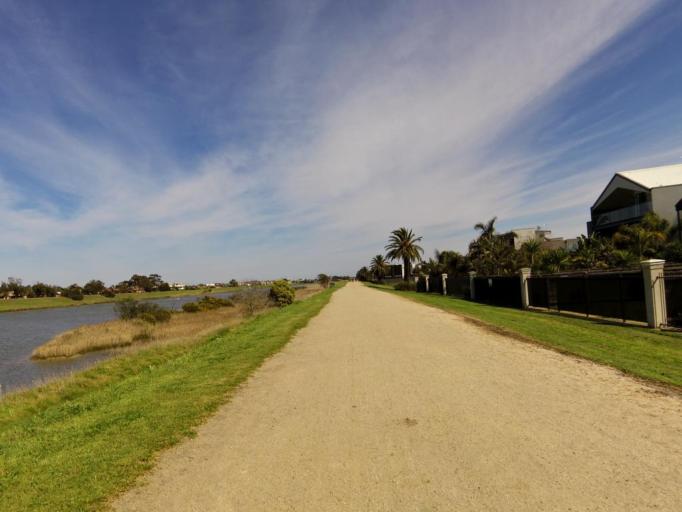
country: AU
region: Victoria
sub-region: Kingston
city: Patterson Lakes
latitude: -38.0589
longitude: 145.1454
